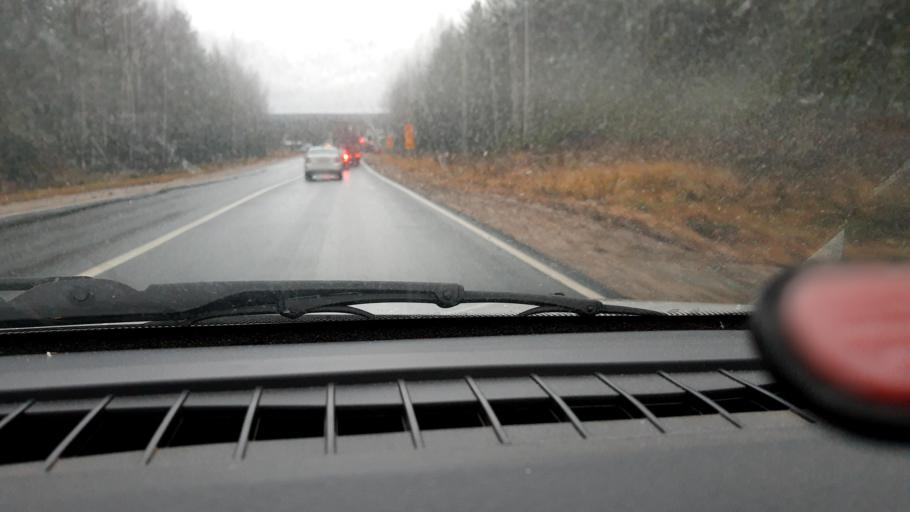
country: RU
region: Nizjnij Novgorod
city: Krasnyye Baki
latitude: 57.1049
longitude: 45.1860
